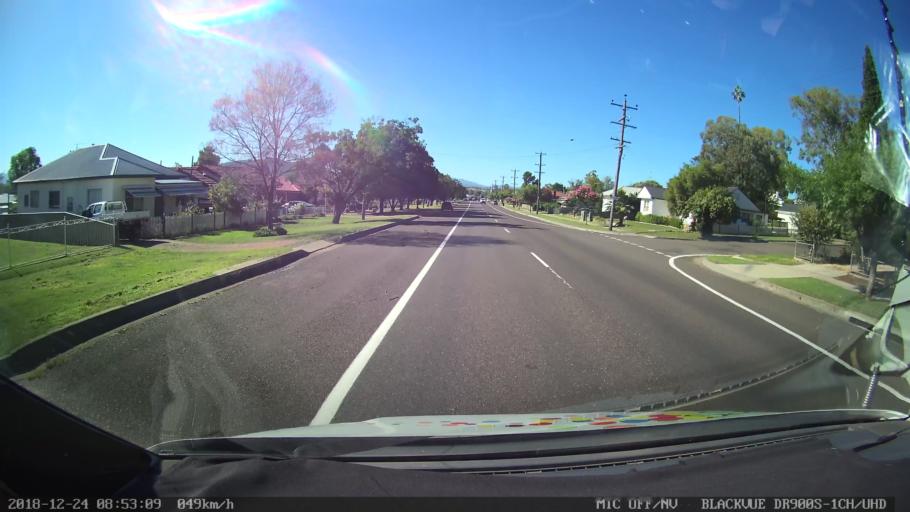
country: AU
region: New South Wales
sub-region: Liverpool Plains
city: Quirindi
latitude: -31.4964
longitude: 150.6810
